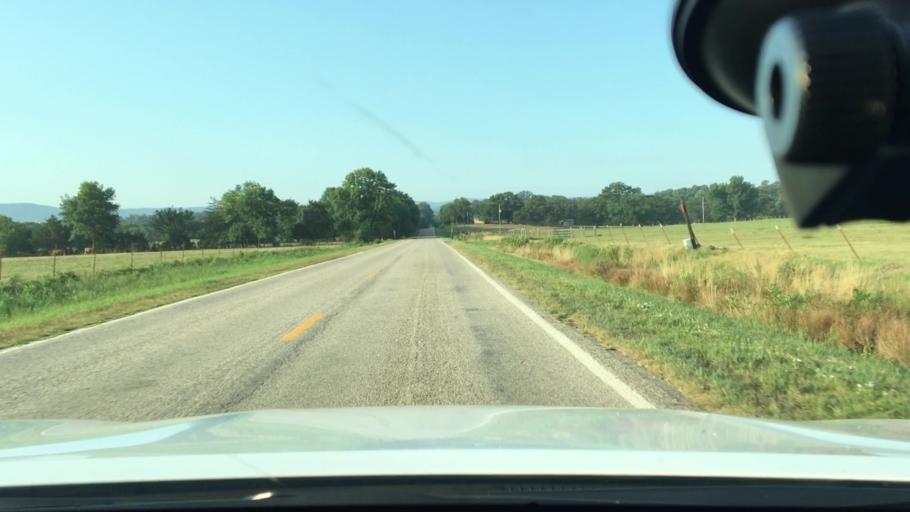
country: US
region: Arkansas
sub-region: Logan County
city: Paris
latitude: 35.3216
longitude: -93.6323
